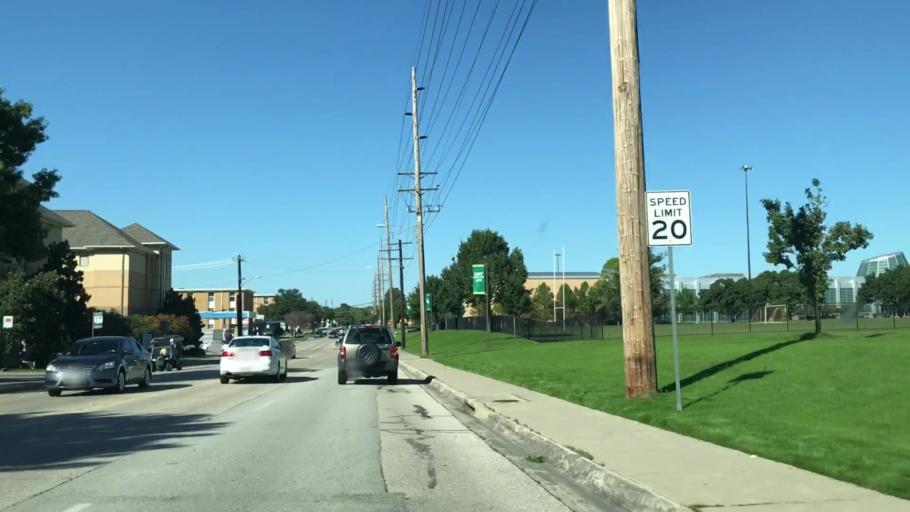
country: US
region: Texas
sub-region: Denton County
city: Denton
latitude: 33.2099
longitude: -97.1550
